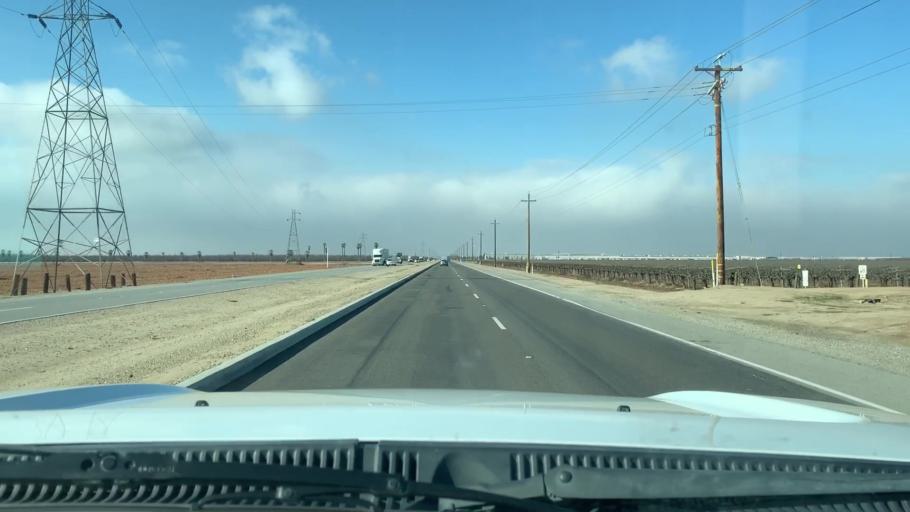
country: US
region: California
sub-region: Kern County
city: Rosedale
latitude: 35.4417
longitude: -119.1630
